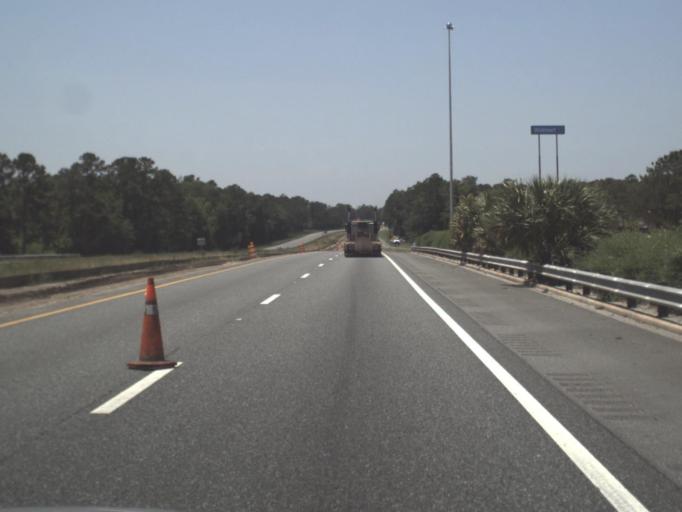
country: US
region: Florida
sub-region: Baker County
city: Macclenny
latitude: 30.2628
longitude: -82.1052
